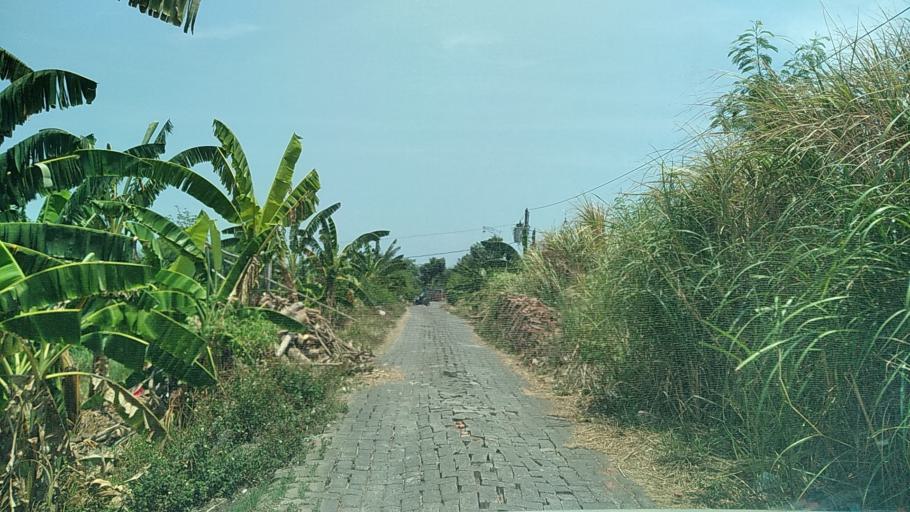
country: ID
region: Central Java
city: Mranggen
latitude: -6.9719
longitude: 110.4972
